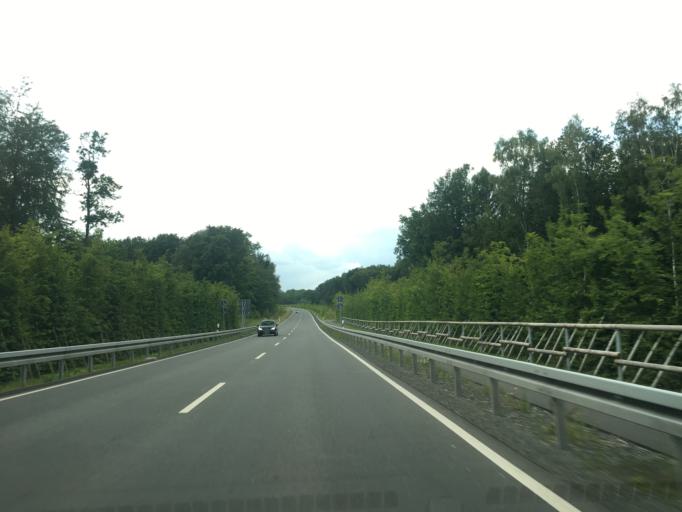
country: DE
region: North Rhine-Westphalia
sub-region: Regierungsbezirk Munster
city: Telgte
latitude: 51.8994
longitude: 7.7320
